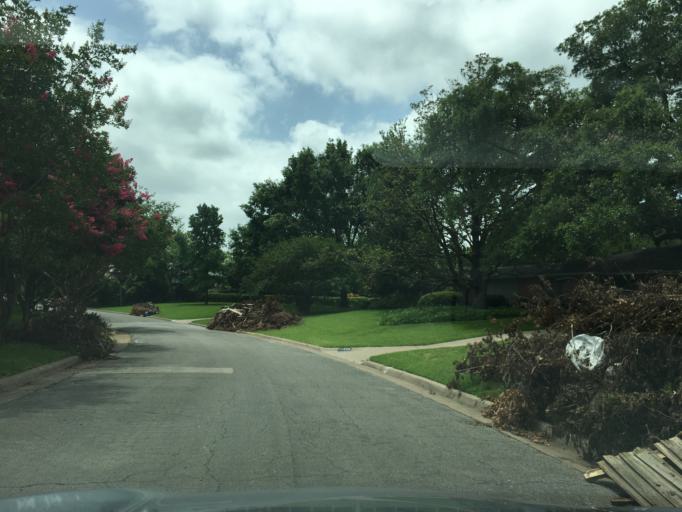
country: US
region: Texas
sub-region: Dallas County
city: University Park
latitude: 32.8987
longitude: -96.7919
